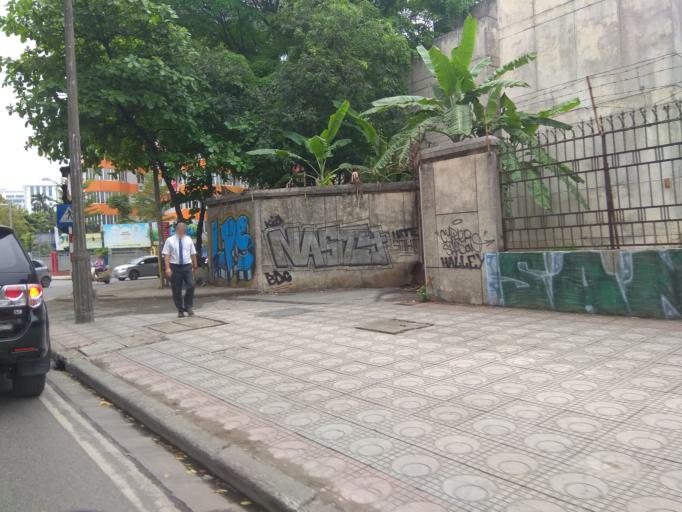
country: VN
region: Ha Noi
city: Cau Giay
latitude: 21.0310
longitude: 105.8175
